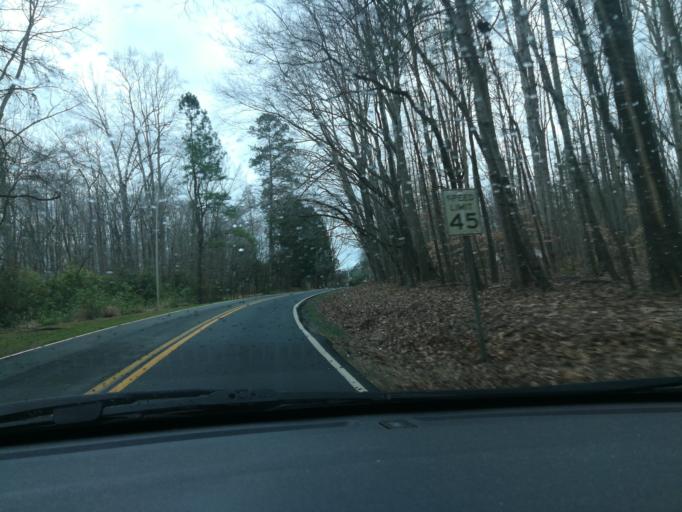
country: US
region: North Carolina
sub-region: Orange County
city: Hillsborough
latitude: 36.0259
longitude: -79.0607
